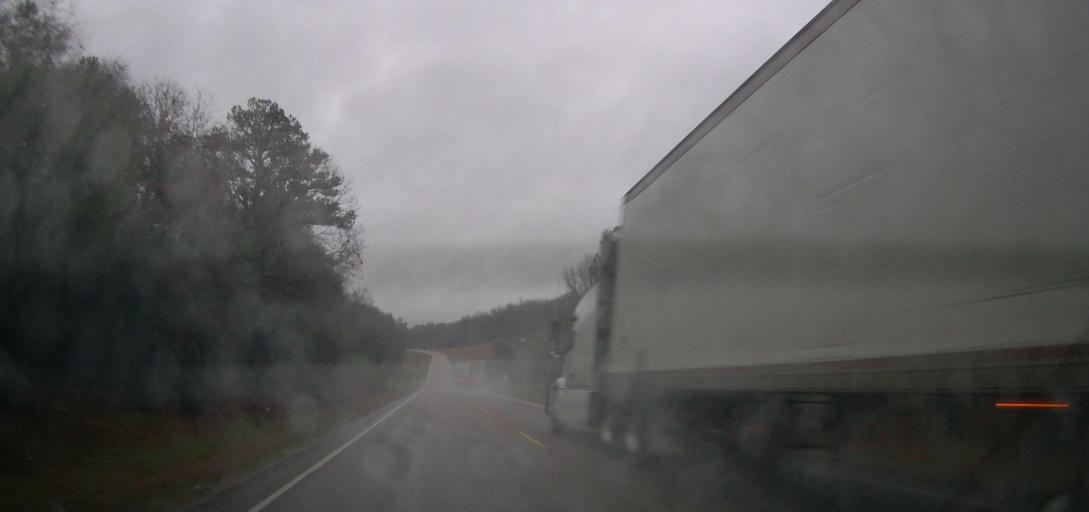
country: US
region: Alabama
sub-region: Autauga County
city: Pine Level
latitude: 32.5264
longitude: -86.6295
